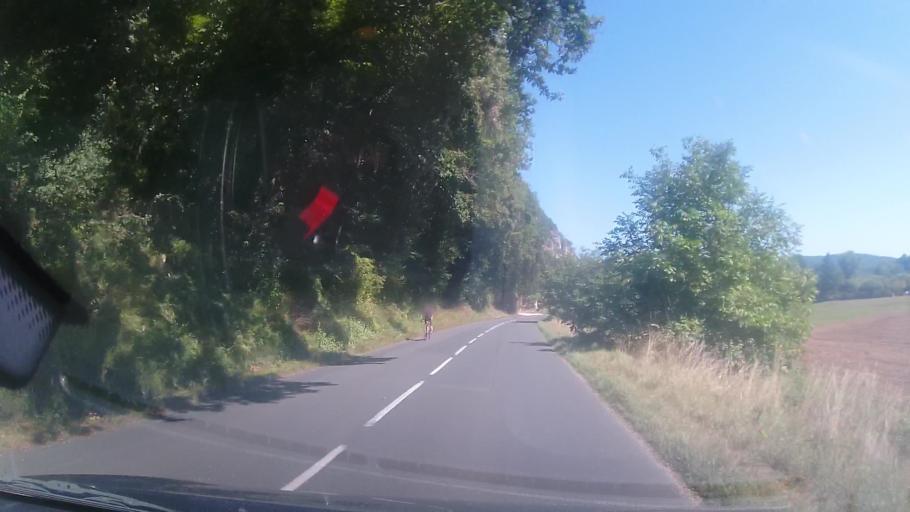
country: FR
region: Aquitaine
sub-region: Departement de la Dordogne
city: Cenac-et-Saint-Julien
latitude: 44.8228
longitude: 1.1666
